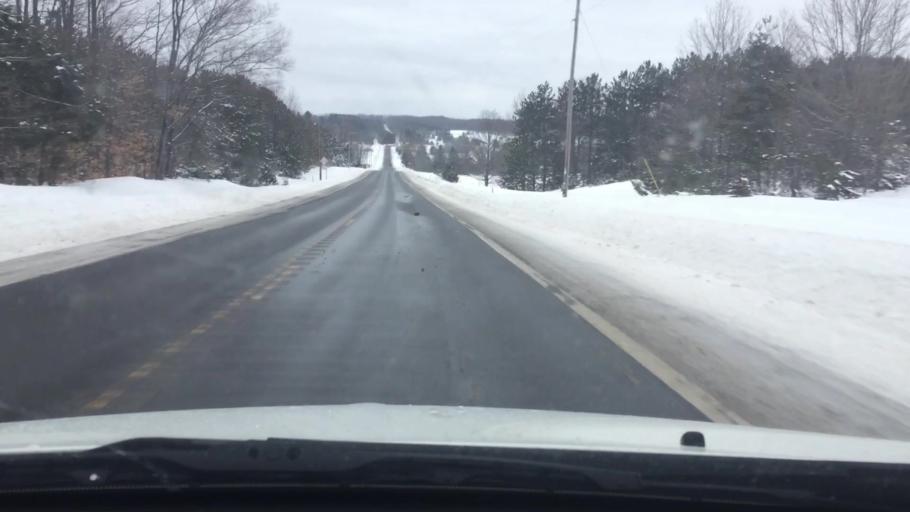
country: US
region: Michigan
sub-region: Charlevoix County
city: East Jordan
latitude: 45.1035
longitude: -85.0326
